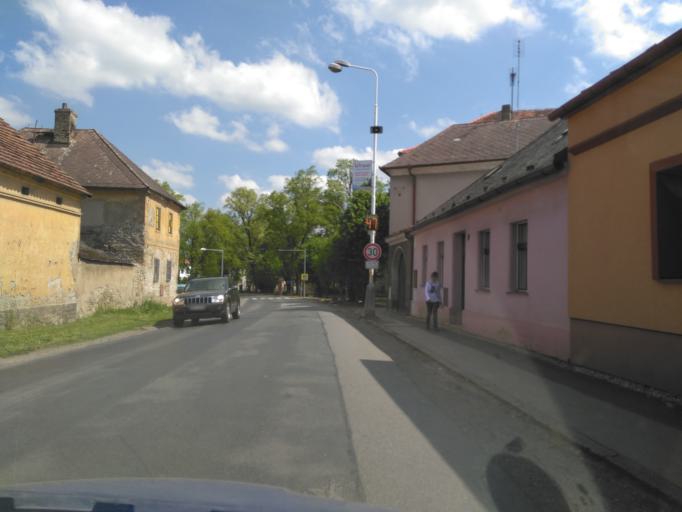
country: CZ
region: Central Bohemia
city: Lochovice
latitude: 49.8509
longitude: 13.9775
